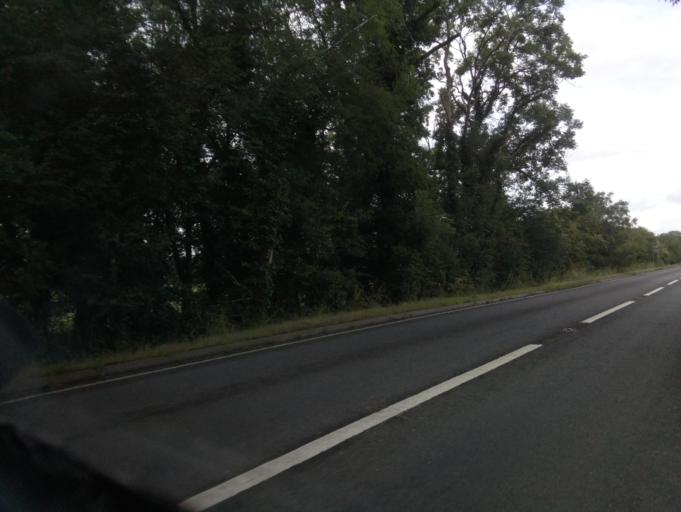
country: GB
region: England
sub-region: Warwickshire
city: Long Itchington
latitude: 52.2749
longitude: -1.3647
